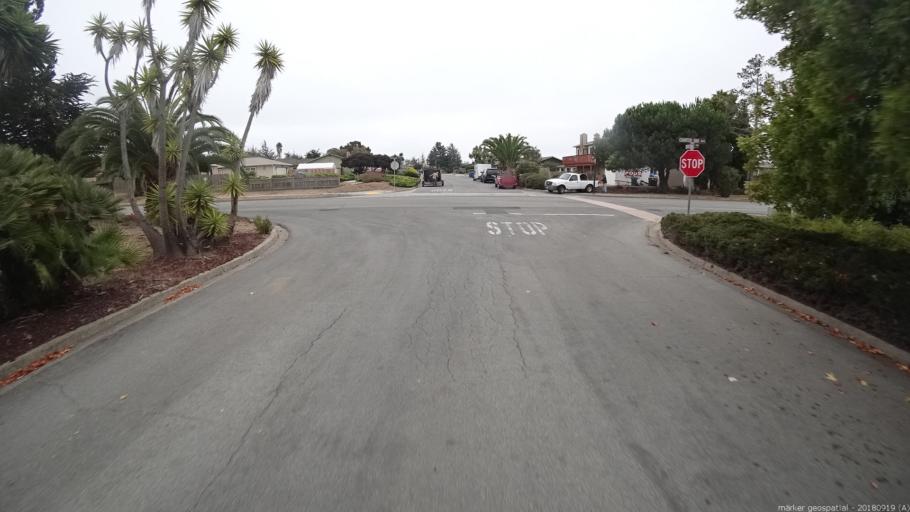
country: US
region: California
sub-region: Monterey County
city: Castroville
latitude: 36.7750
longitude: -121.7284
